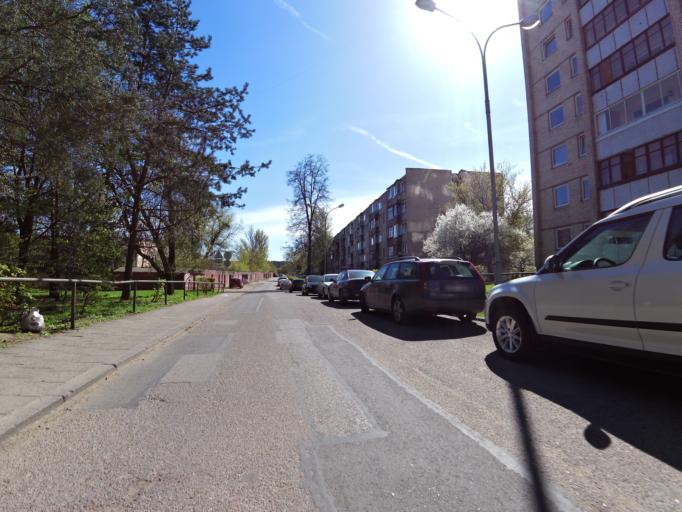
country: LT
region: Vilnius County
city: Vilkpede
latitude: 54.6706
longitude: 25.2544
